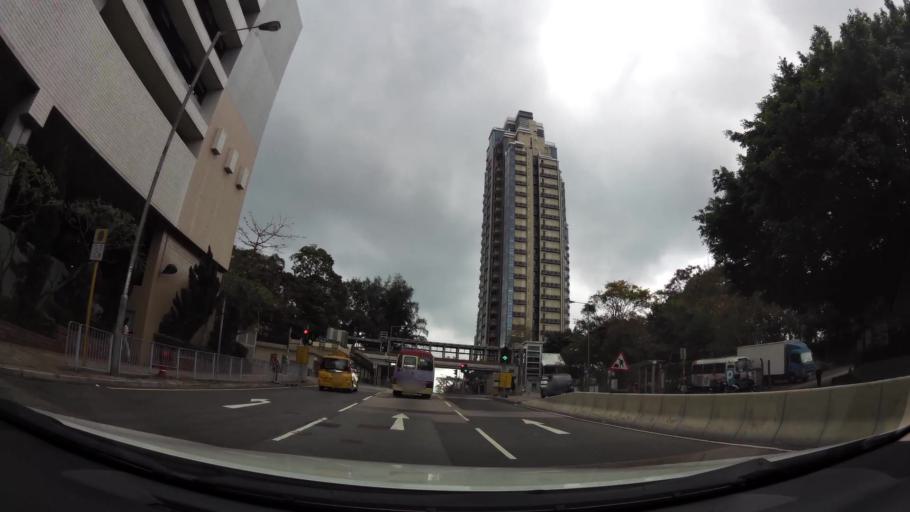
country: HK
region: Kowloon City
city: Kowloon
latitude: 22.3139
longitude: 114.1818
